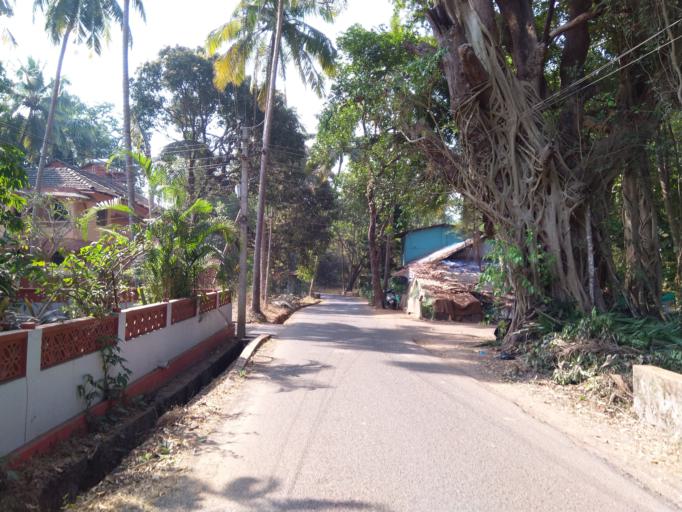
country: IN
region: Goa
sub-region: North Goa
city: Saligao
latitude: 15.5639
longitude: 73.7690
